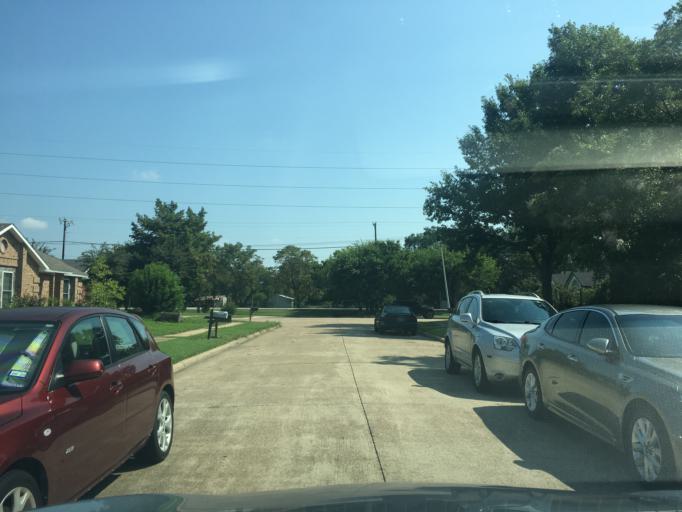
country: US
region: Texas
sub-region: Dallas County
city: Sachse
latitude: 32.9497
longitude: -96.6243
